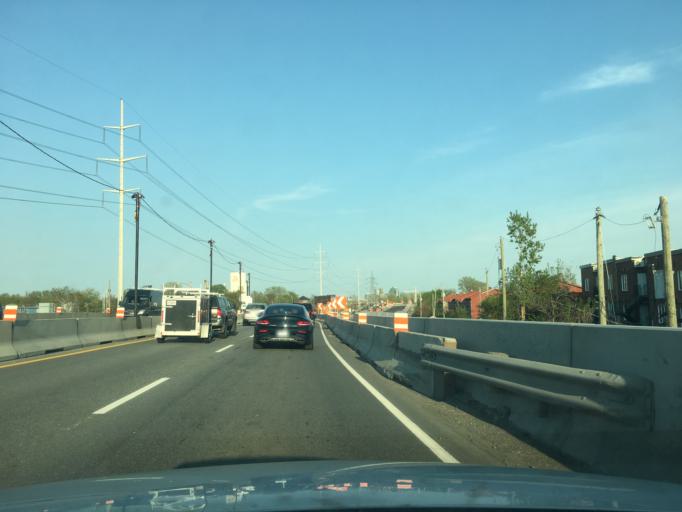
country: CA
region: Quebec
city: Westmount
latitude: 45.4747
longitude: -73.5698
